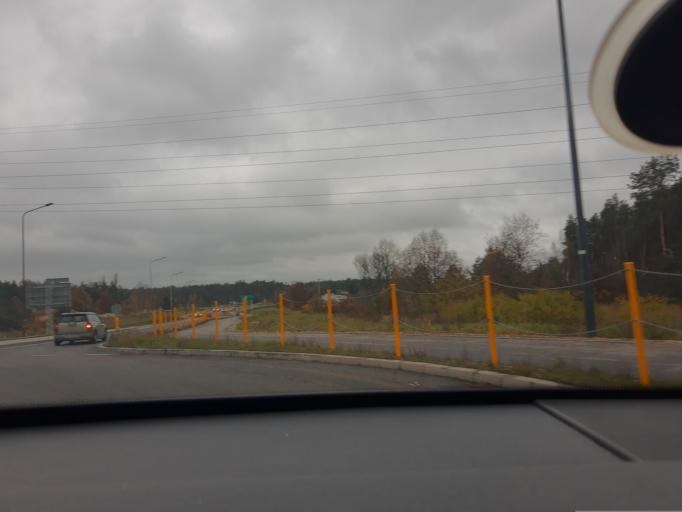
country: PL
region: Lodz Voivodeship
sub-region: Powiat pabianicki
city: Konstantynow Lodzki
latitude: 51.7286
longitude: 19.3537
